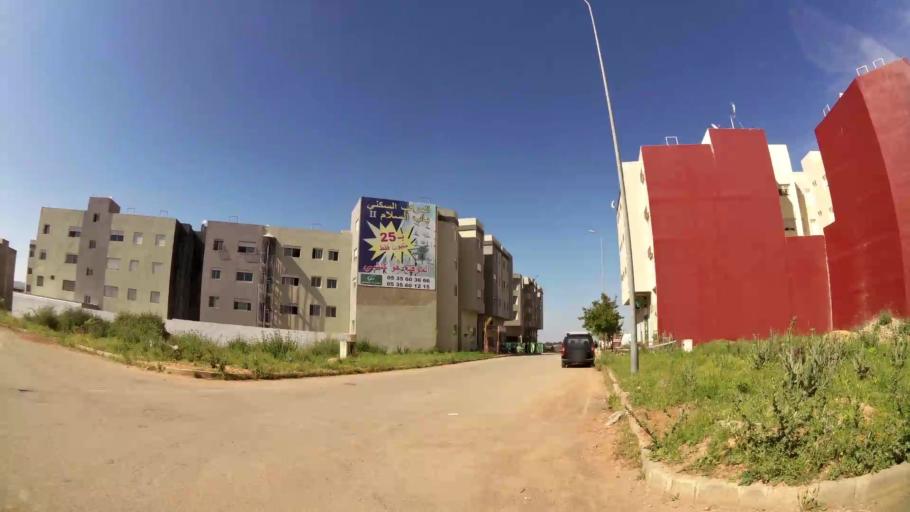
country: MA
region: Fes-Boulemane
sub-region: Fes
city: Fes
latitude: 33.9950
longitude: -5.0045
